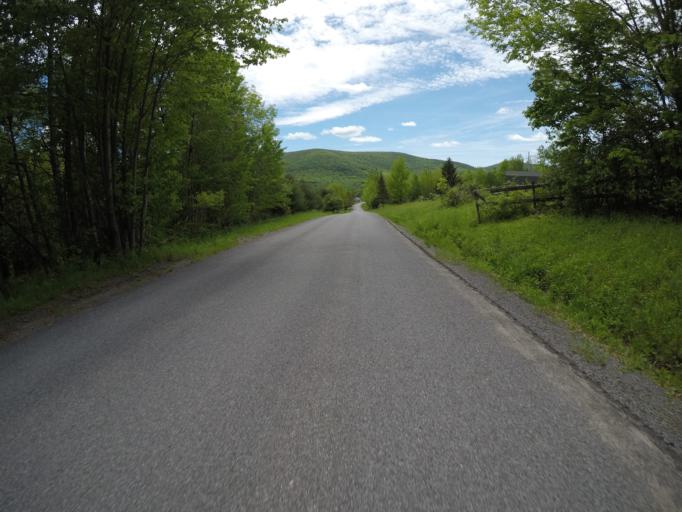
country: US
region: New York
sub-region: Delaware County
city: Stamford
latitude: 42.2716
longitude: -74.5195
